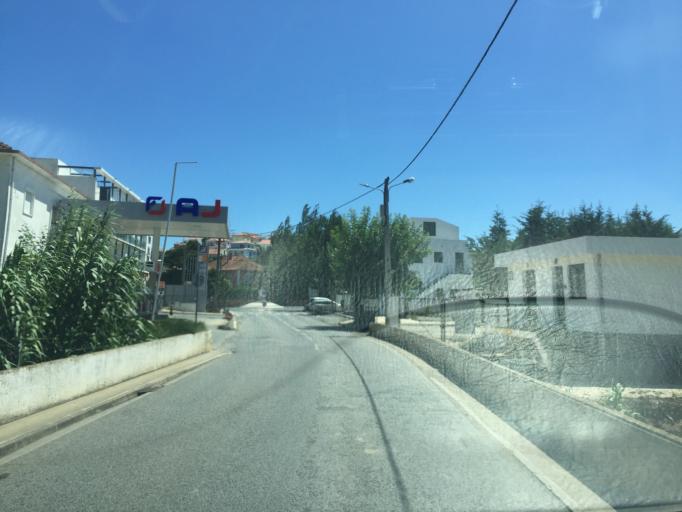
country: PT
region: Lisbon
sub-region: Torres Vedras
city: A dos Cunhados
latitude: 39.1771
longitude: -9.3223
